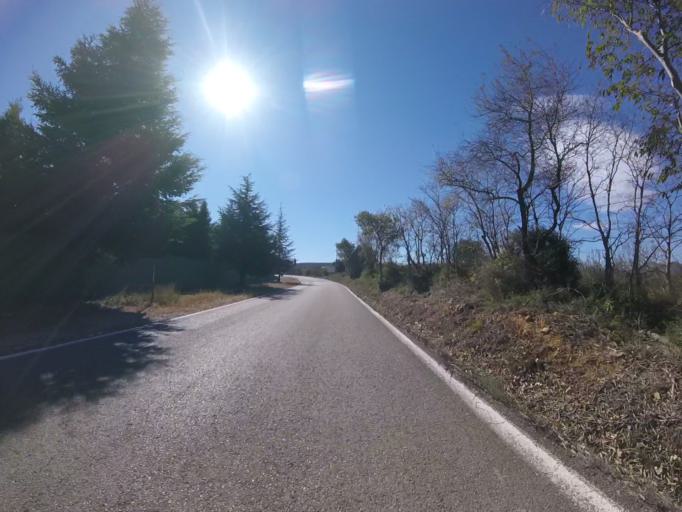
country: ES
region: Valencia
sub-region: Provincia de Castello
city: Albocasser
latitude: 40.3657
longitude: 0.0206
